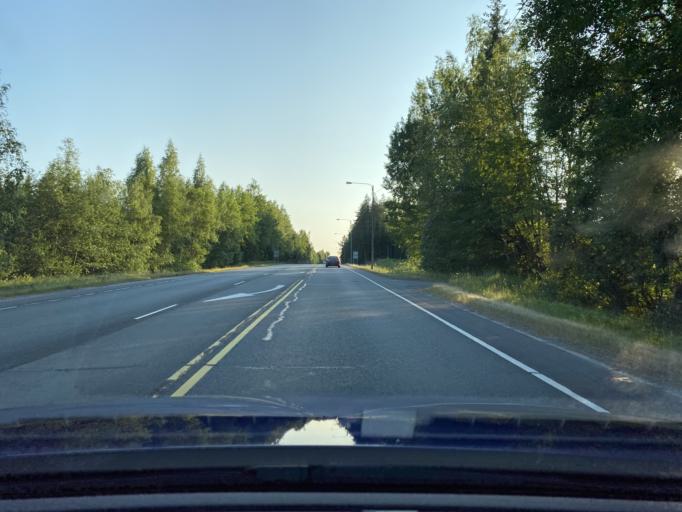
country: FI
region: Haeme
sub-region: Forssa
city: Forssa
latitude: 60.8289
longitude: 23.6600
